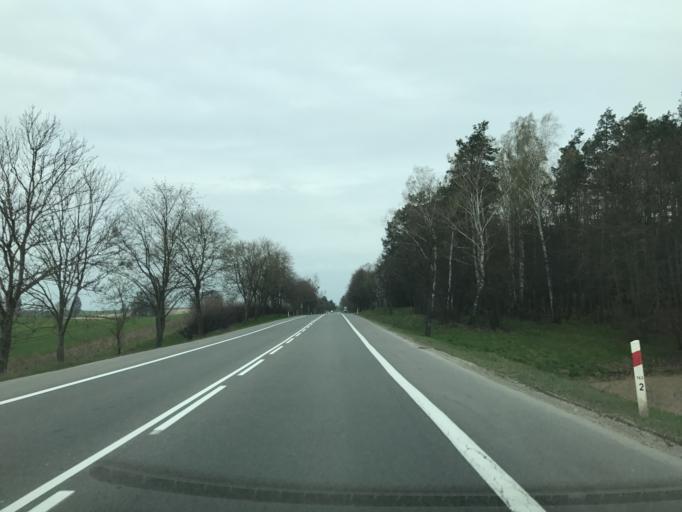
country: PL
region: Warmian-Masurian Voivodeship
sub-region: Powiat ostrodzki
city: Gierzwald
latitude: 53.6037
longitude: 20.0747
